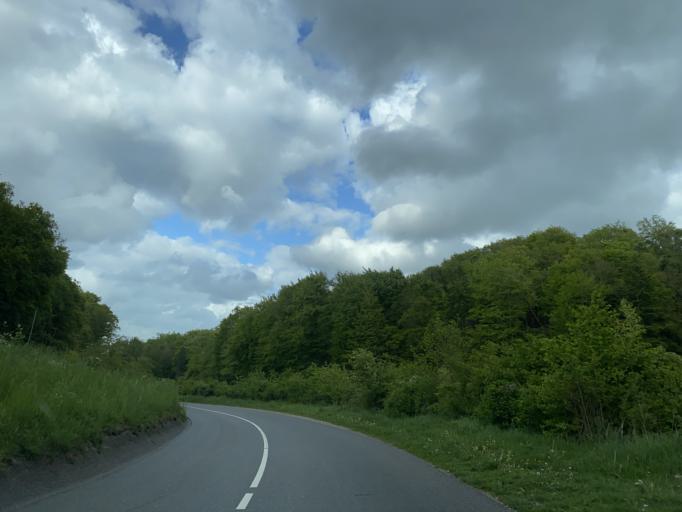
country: DK
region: Central Jutland
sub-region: Horsens Kommune
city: Braedstrup
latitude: 56.0250
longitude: 9.6471
